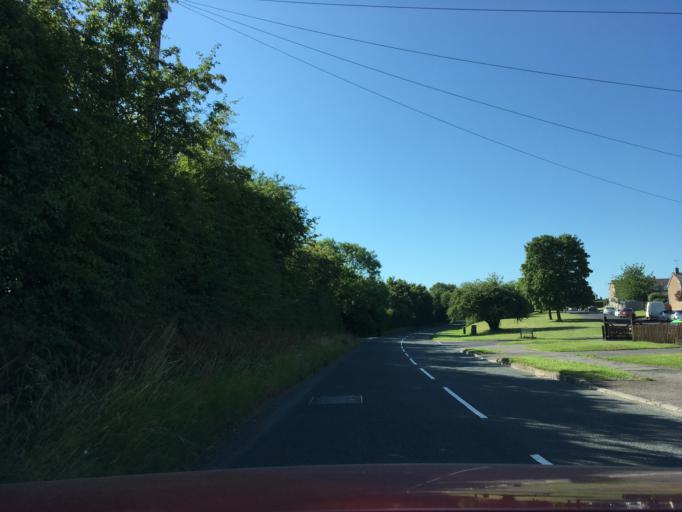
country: GB
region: England
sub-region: South Gloucestershire
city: Pucklechurch
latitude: 51.4842
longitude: -2.4292
